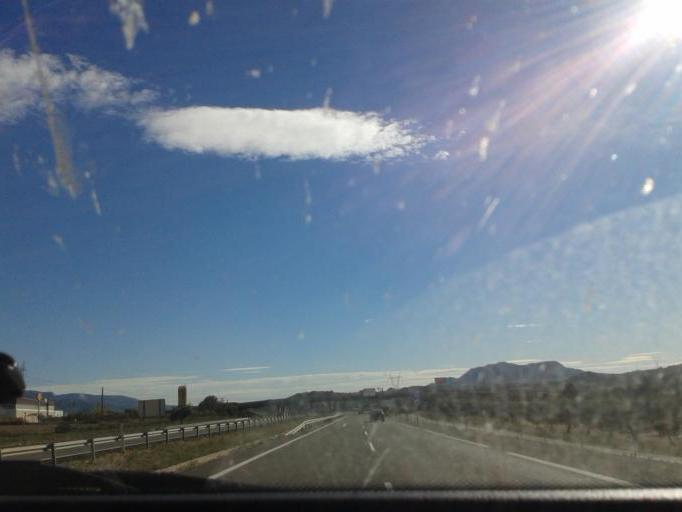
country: ES
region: Valencia
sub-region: Provincia de Alicante
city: Sax
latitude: 38.5774
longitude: -0.8418
